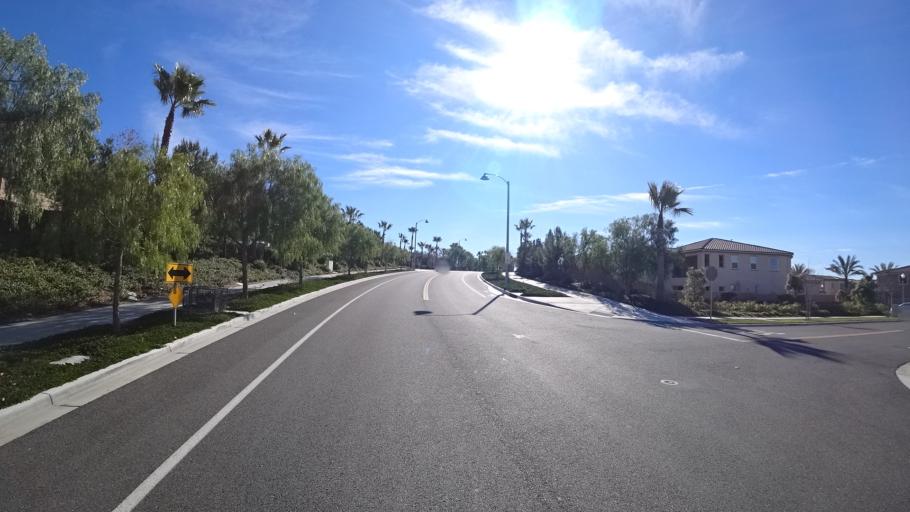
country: US
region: California
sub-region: Orange County
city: Foothill Ranch
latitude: 33.6745
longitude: -117.6763
